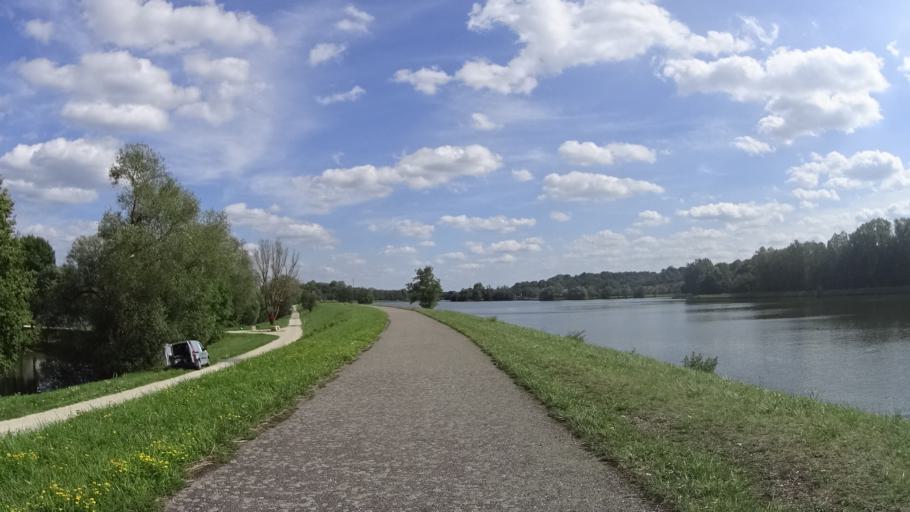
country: FR
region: Lorraine
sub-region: Departement de Meurthe-et-Moselle
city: Dommartin-les-Toul
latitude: 48.6646
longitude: 5.8923
